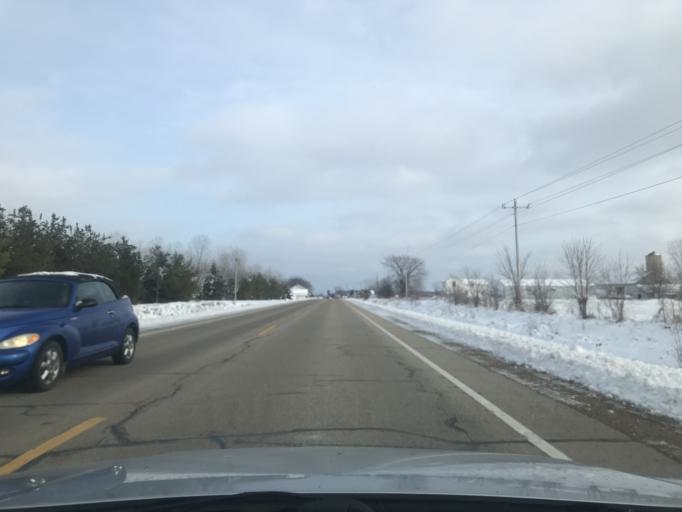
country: US
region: Wisconsin
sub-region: Oconto County
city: Oconto
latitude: 44.8927
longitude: -87.9627
